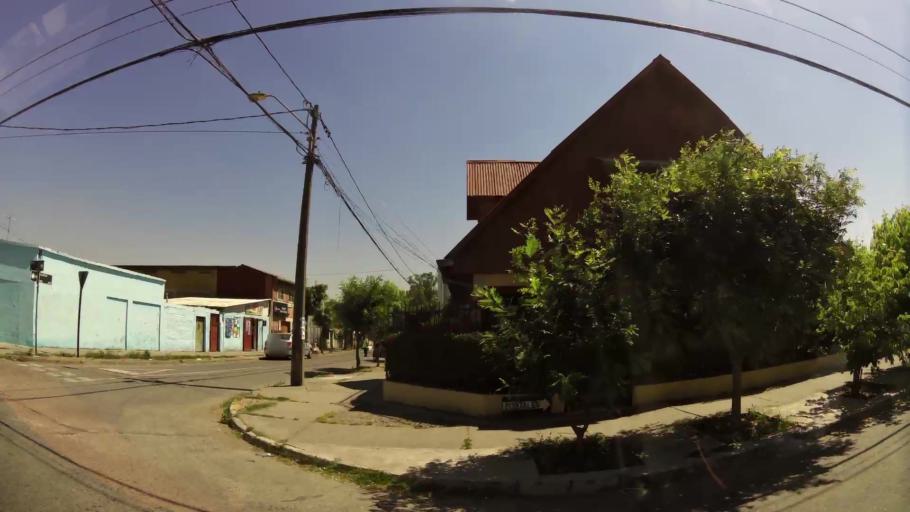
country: CL
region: Santiago Metropolitan
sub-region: Provincia de Santiago
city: La Pintana
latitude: -33.5618
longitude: -70.6668
